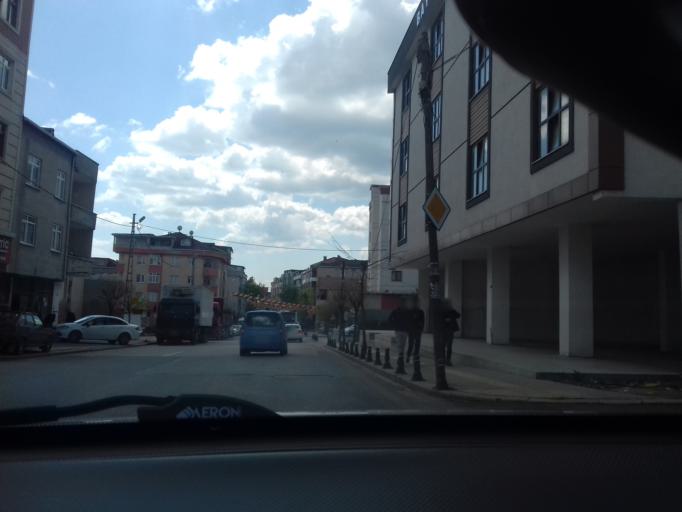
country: TR
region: Istanbul
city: Pendik
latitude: 40.8858
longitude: 29.2864
